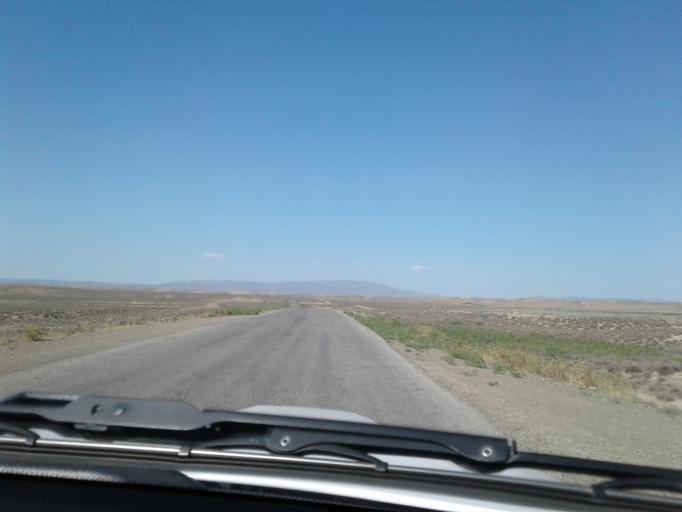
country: TM
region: Balkan
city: Magtymguly
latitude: 38.6161
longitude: 56.2231
